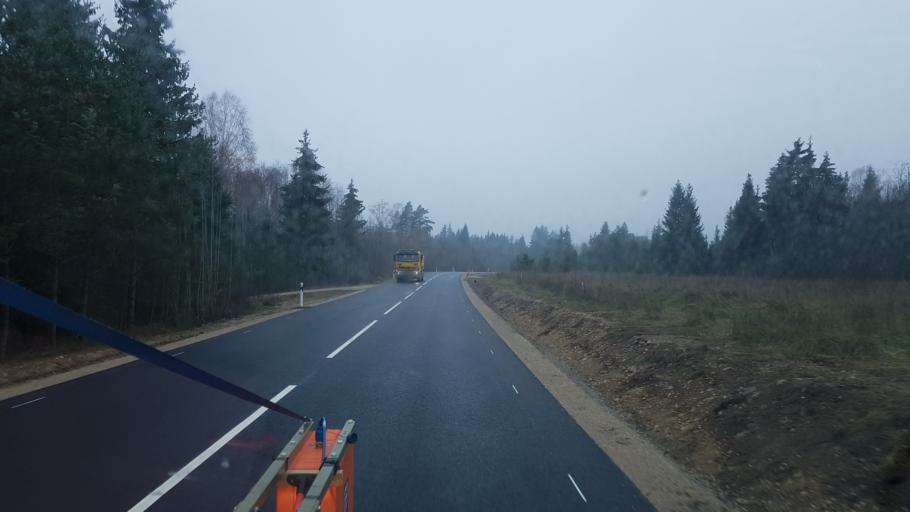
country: EE
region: Raplamaa
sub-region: Kohila vald
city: Kohila
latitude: 59.1765
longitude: 24.8313
